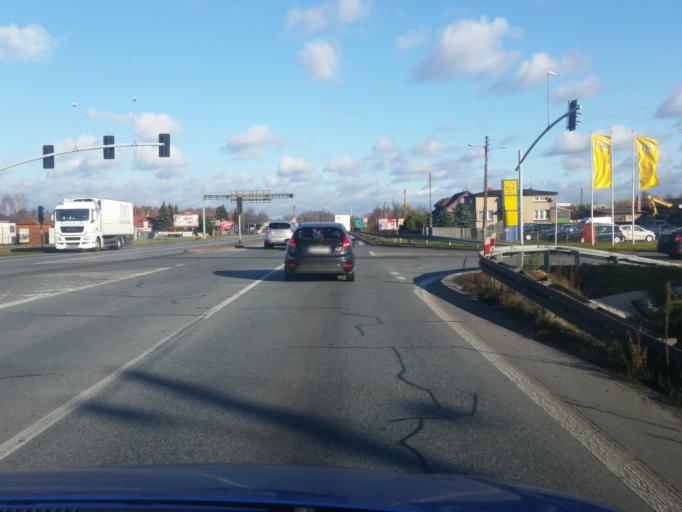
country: PL
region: Silesian Voivodeship
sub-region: Powiat czestochowski
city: Huta Stara B
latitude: 50.7053
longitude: 19.1447
